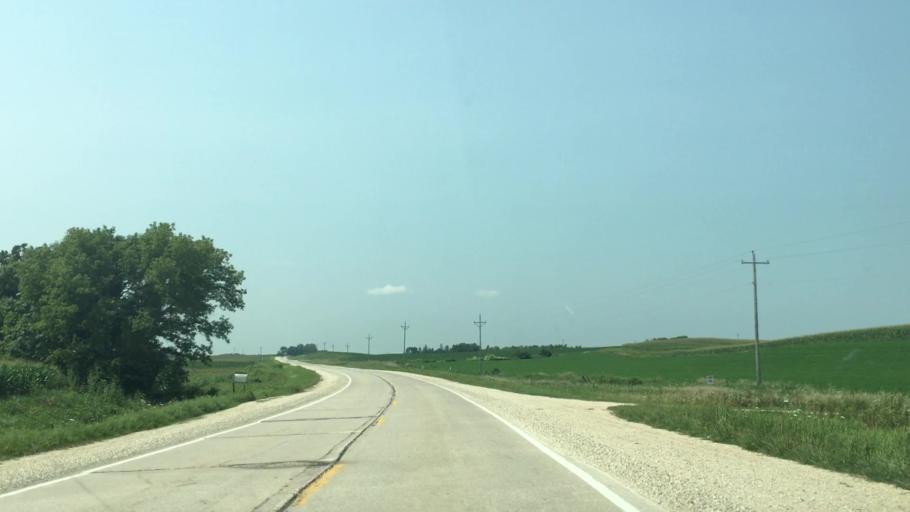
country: US
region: Iowa
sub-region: Fayette County
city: West Union
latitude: 43.0928
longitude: -91.8568
